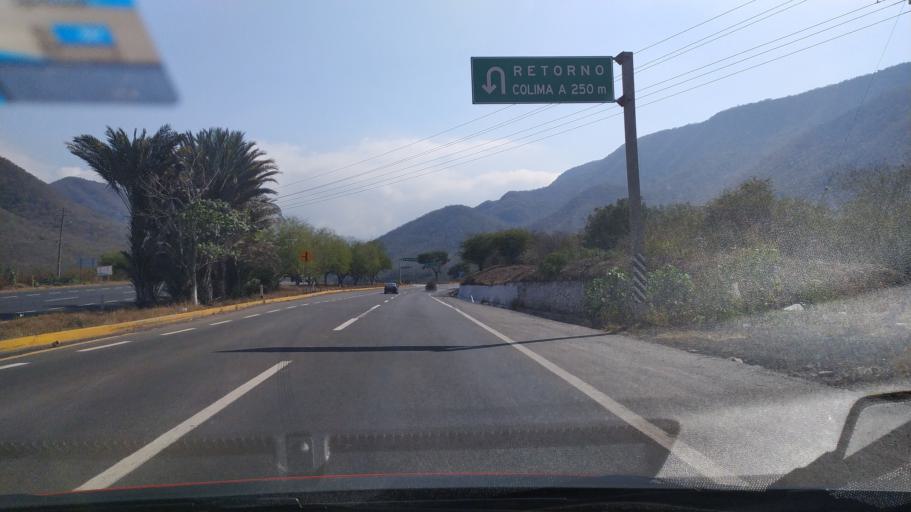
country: MX
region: Colima
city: Madrid
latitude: 19.1054
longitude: -103.7763
